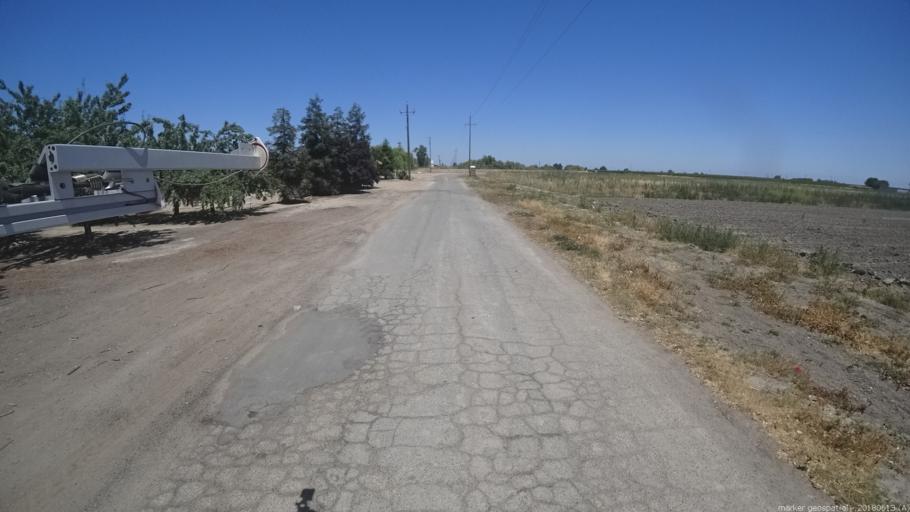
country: US
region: California
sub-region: Madera County
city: Chowchilla
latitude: 37.0076
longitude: -120.3286
